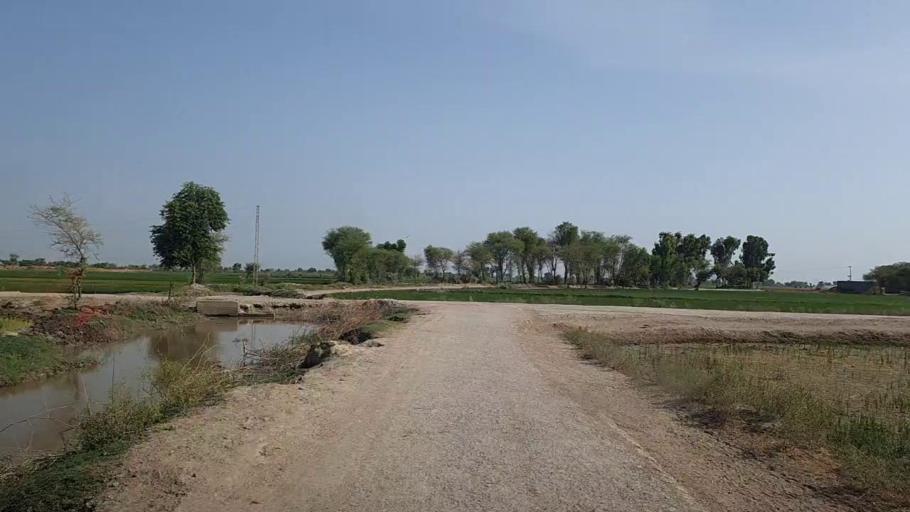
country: PK
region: Sindh
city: Sita Road
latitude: 27.0956
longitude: 67.8529
